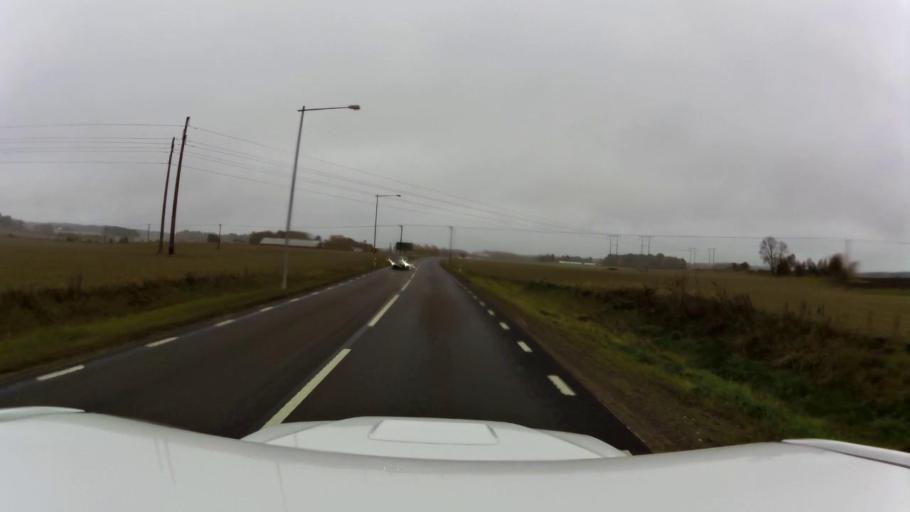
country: SE
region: OEstergoetland
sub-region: Linkopings Kommun
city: Linghem
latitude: 58.3962
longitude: 15.7689
